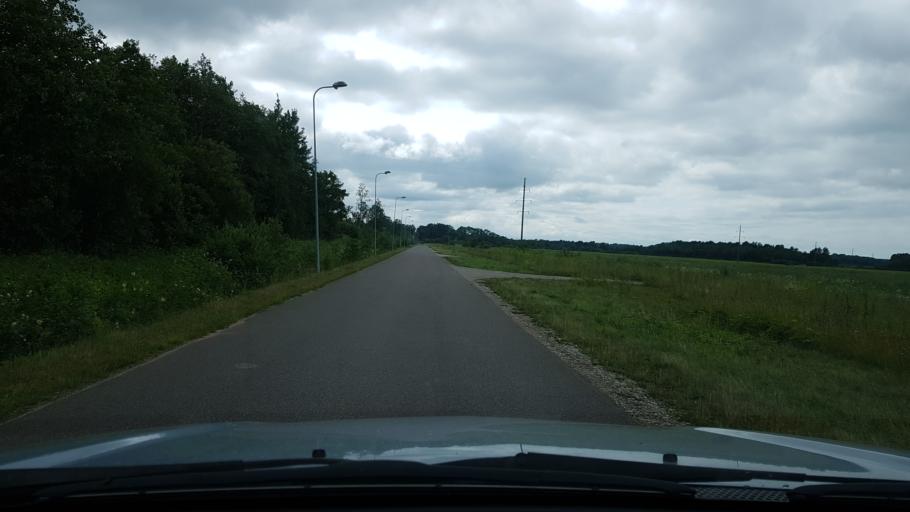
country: EE
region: Ida-Virumaa
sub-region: Narva linn
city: Narva
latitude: 59.3952
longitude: 28.1204
